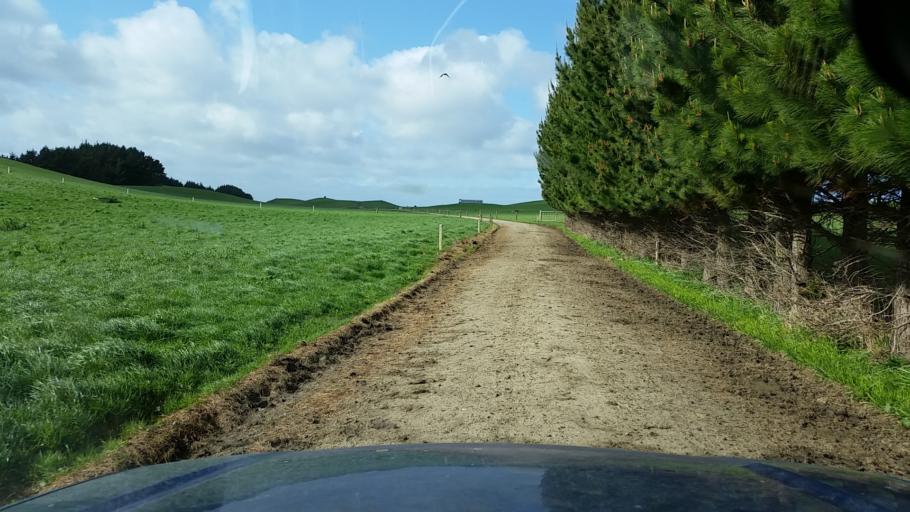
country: NZ
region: Taranaki
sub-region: South Taranaki District
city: Patea
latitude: -39.7411
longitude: 174.5293
